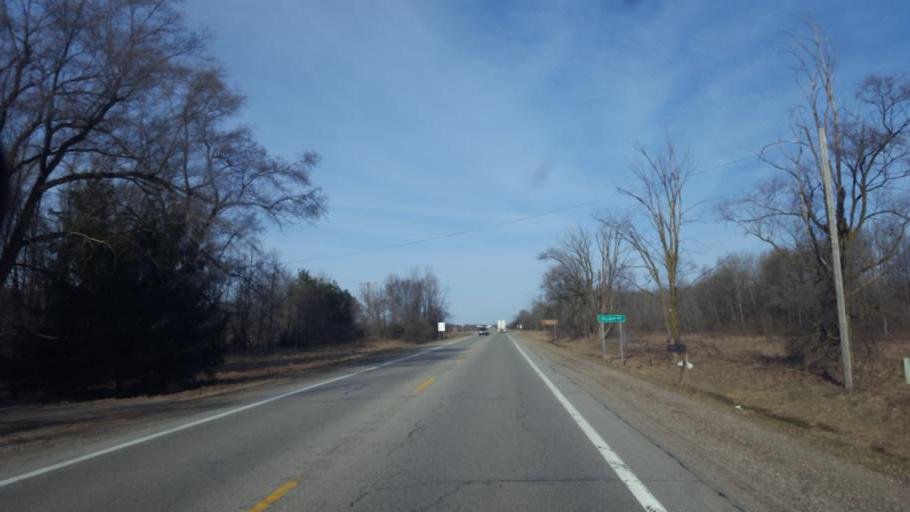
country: US
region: Michigan
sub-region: Montcalm County
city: Lakeview
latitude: 43.4301
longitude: -85.1804
